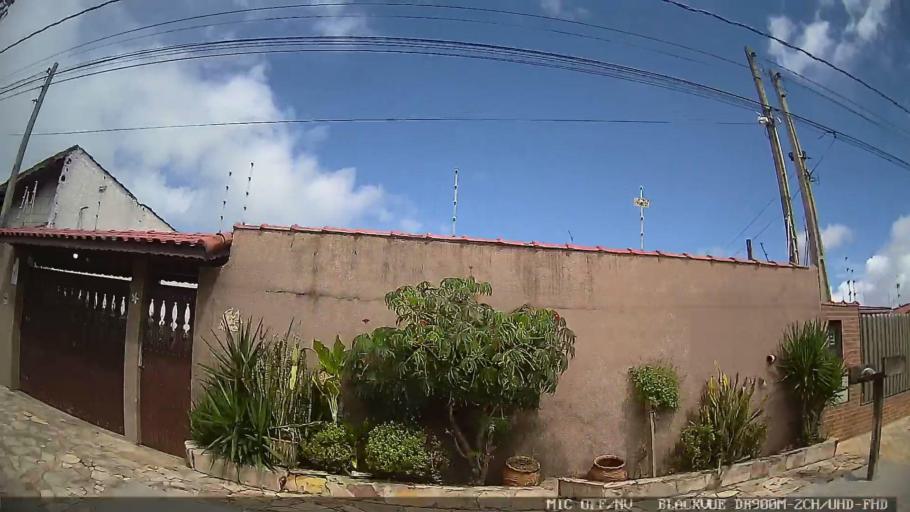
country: BR
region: Sao Paulo
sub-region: Itanhaem
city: Itanhaem
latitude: -24.2281
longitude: -46.8635
